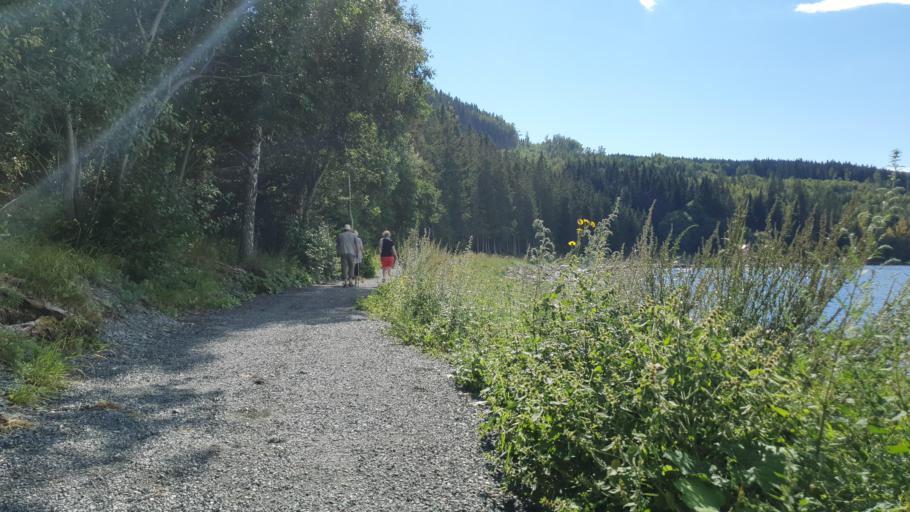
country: NO
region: Nord-Trondelag
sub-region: Levanger
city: Levanger
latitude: 63.7739
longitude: 11.3764
